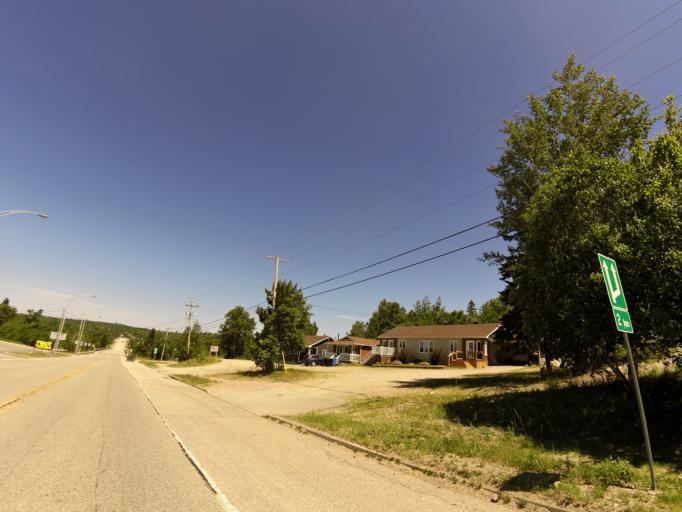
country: CA
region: Quebec
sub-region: Abitibi-Temiscamingue
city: Temiscaming
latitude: 46.7381
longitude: -79.0665
